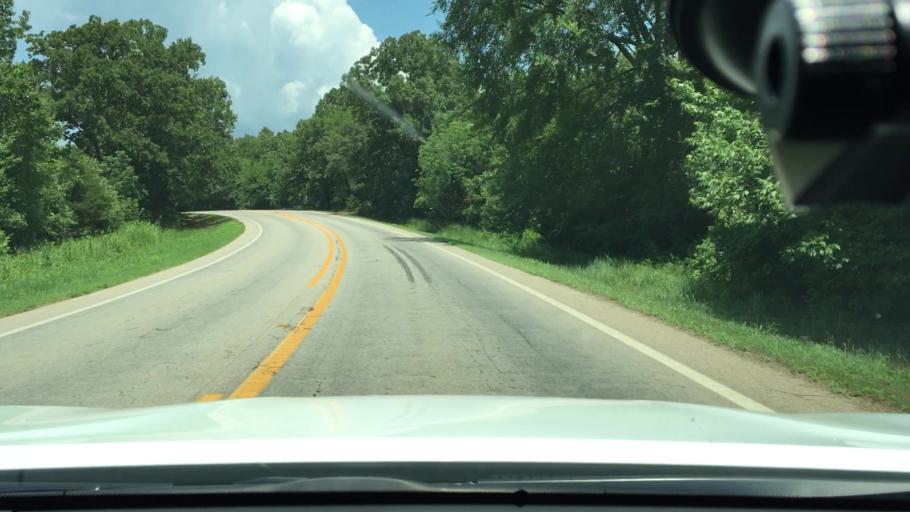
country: US
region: Arkansas
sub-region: Logan County
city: Booneville
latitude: 35.2080
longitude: -93.9245
